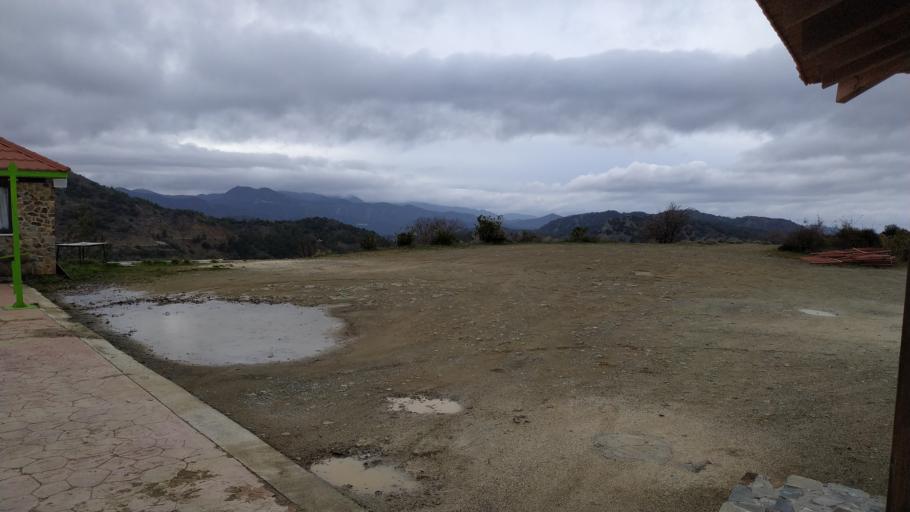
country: CY
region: Lefkosia
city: Kakopetria
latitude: 34.9707
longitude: 32.8242
